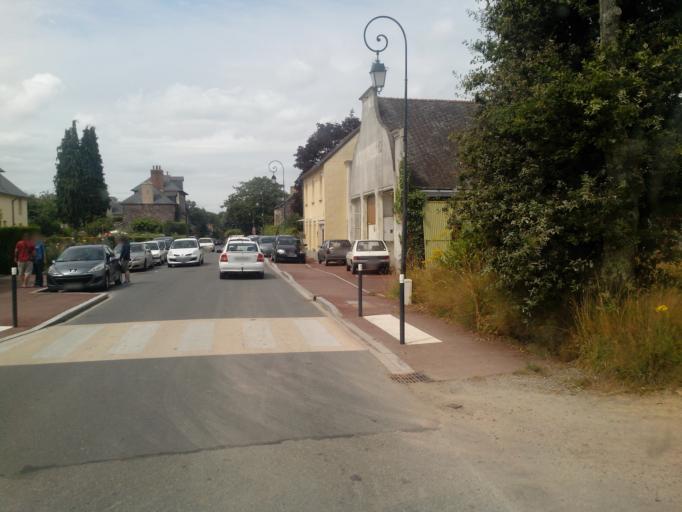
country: FR
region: Brittany
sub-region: Departement d'Ille-et-Vilaine
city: Paimpont
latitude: 48.0177
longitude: -2.1701
